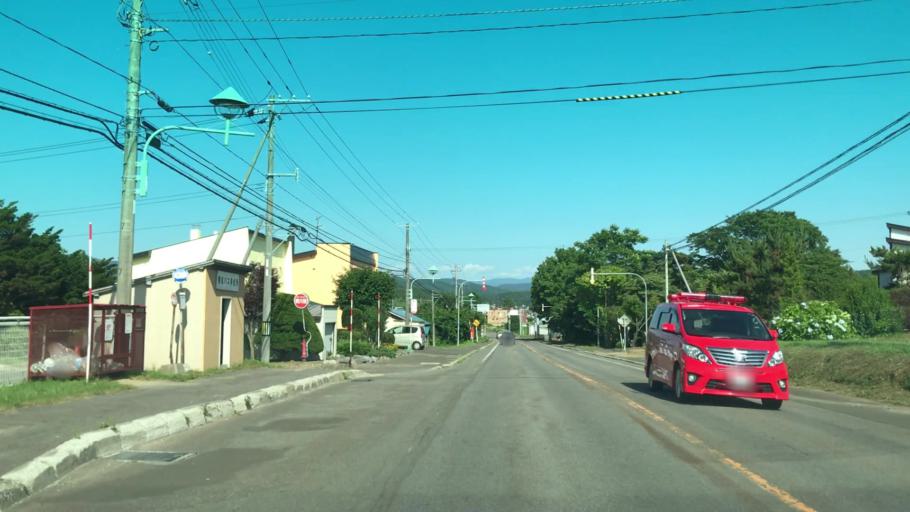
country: JP
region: Hokkaido
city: Iwanai
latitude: 42.9798
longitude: 140.6060
